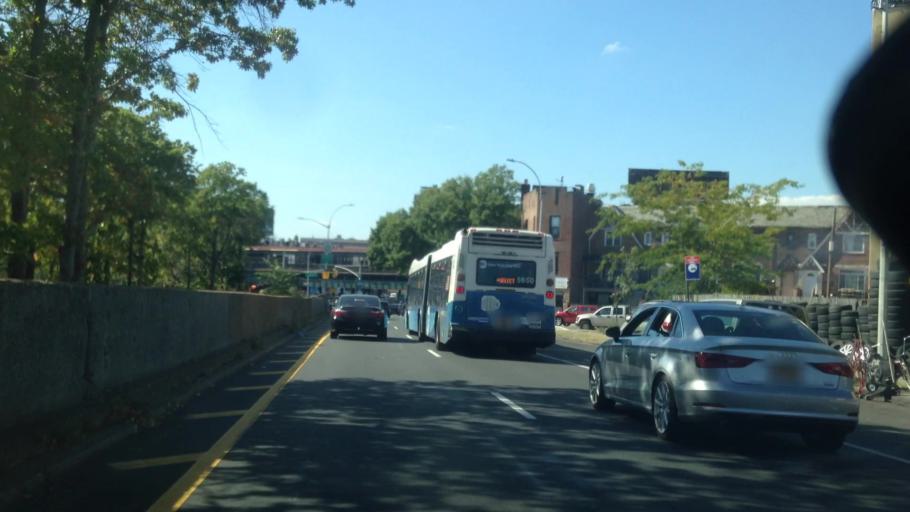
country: US
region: New York
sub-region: Queens County
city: Long Island City
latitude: 40.7701
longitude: -73.9150
